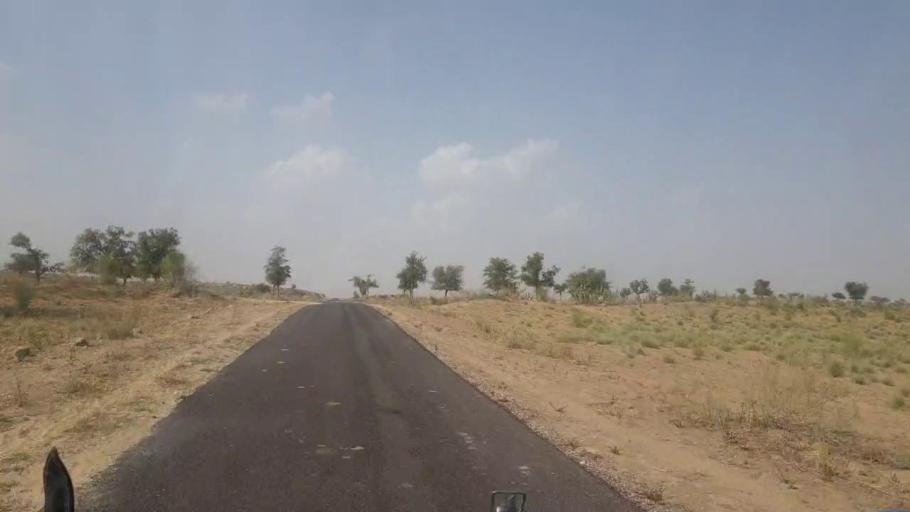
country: PK
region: Sindh
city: Islamkot
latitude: 25.1894
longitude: 70.2857
